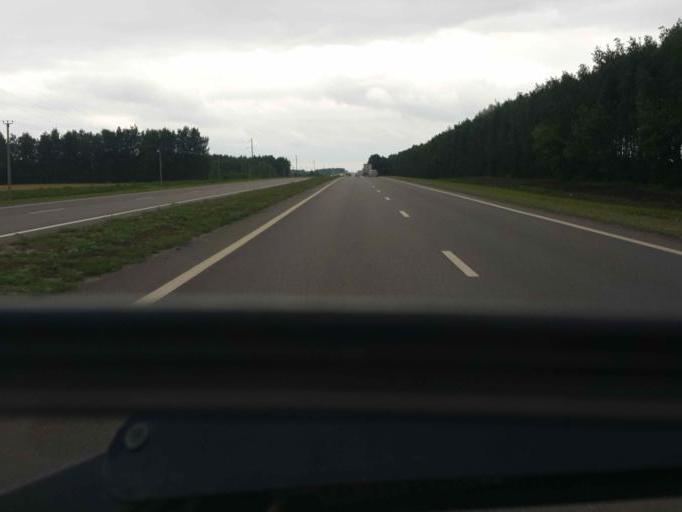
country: RU
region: Tambov
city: Zavoronezhskoye
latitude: 52.8805
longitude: 40.7366
